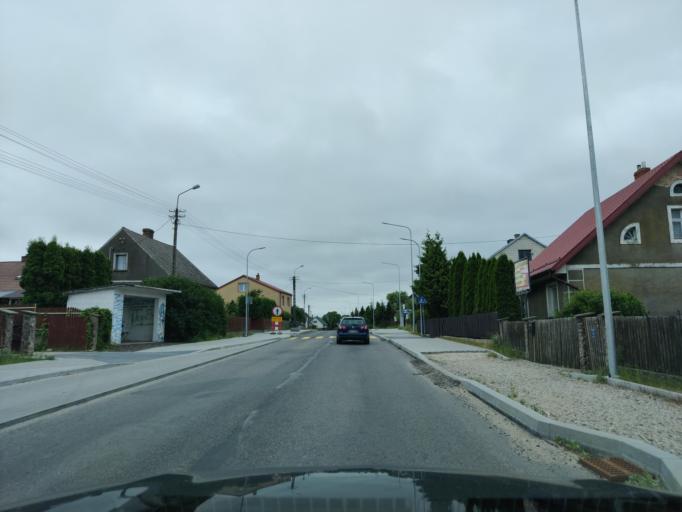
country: PL
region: Warmian-Masurian Voivodeship
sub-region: Powiat szczycienski
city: Rozogi
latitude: 53.4383
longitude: 21.3700
